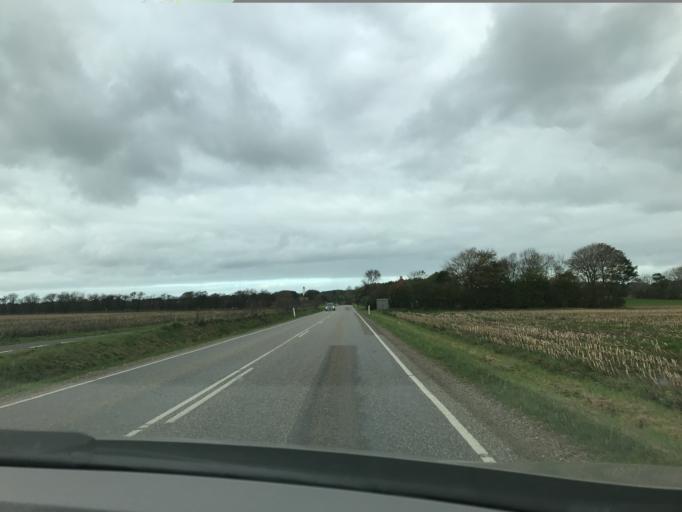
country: DK
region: South Denmark
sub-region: Varde Kommune
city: Olgod
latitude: 55.7993
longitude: 8.6407
